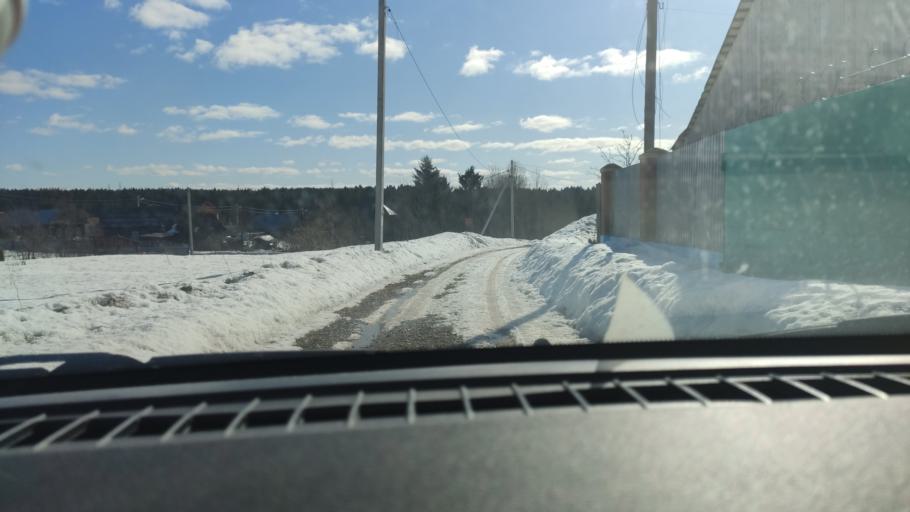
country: RU
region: Perm
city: Perm
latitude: 58.0367
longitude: 56.3983
